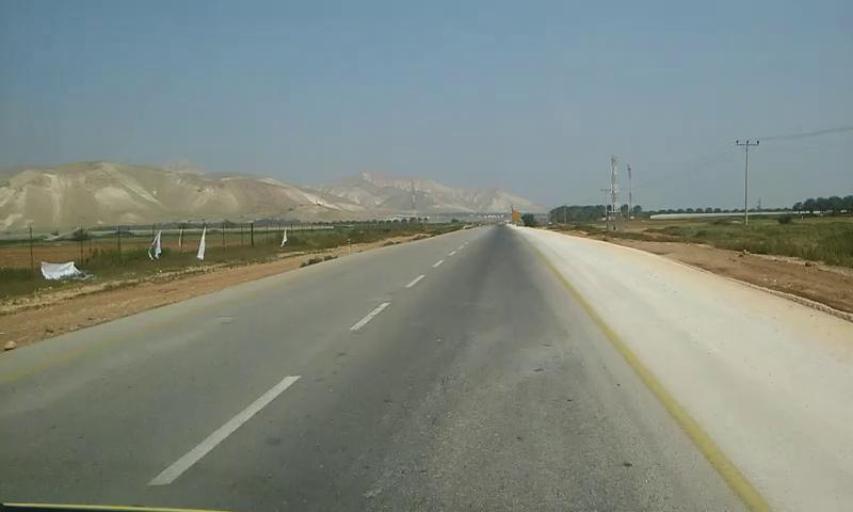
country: PS
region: West Bank
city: Al Fasayil
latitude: 32.0386
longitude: 35.4577
